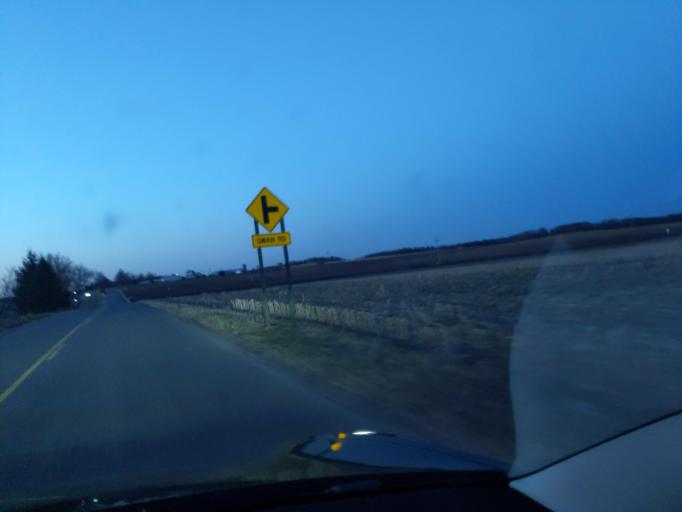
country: US
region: Michigan
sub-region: Ingham County
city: Stockbridge
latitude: 42.5179
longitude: -84.2199
